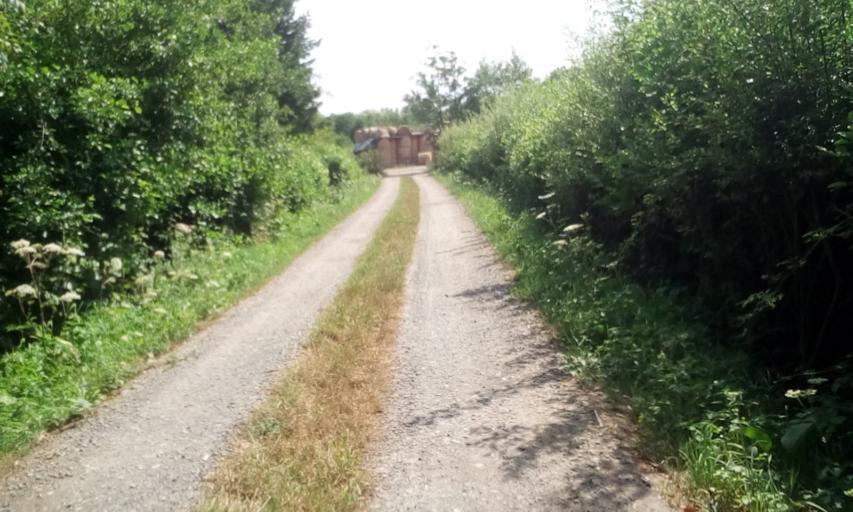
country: FR
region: Lower Normandy
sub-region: Departement du Calvados
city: Bavent
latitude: 49.2404
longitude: -0.1714
